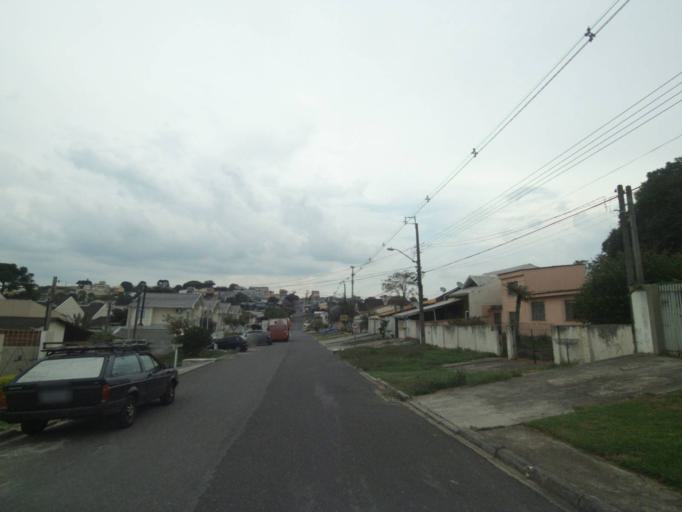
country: BR
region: Parana
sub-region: Pinhais
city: Pinhais
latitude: -25.3967
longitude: -49.2047
